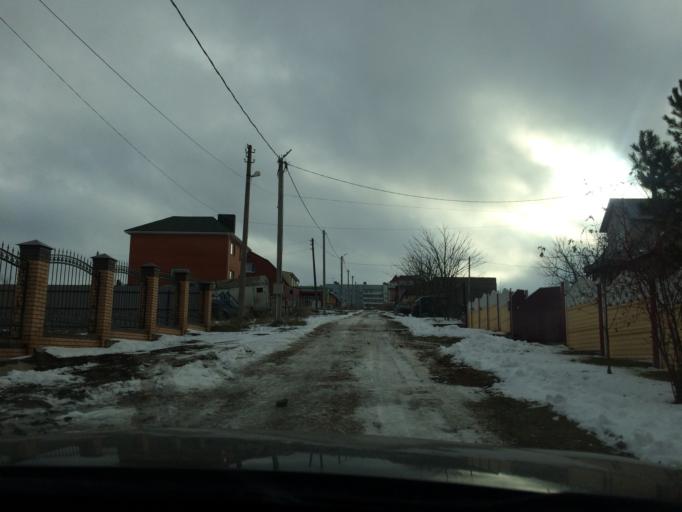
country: RU
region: Tula
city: Plavsk
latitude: 53.7062
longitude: 37.2714
